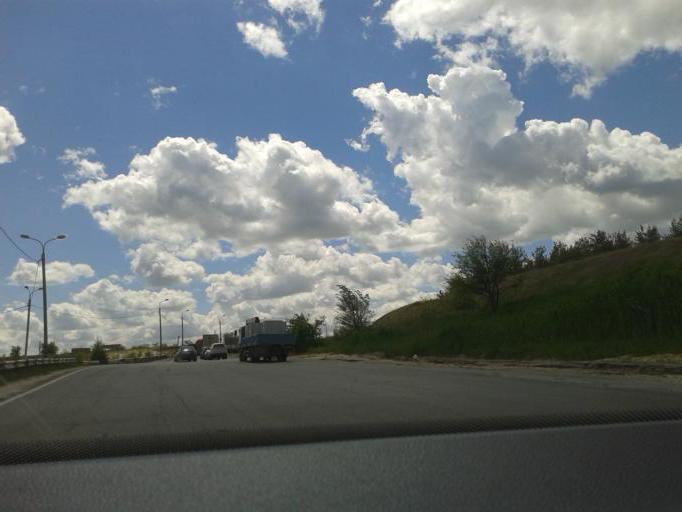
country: RU
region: Volgograd
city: Volgograd
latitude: 48.7071
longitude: 44.4412
